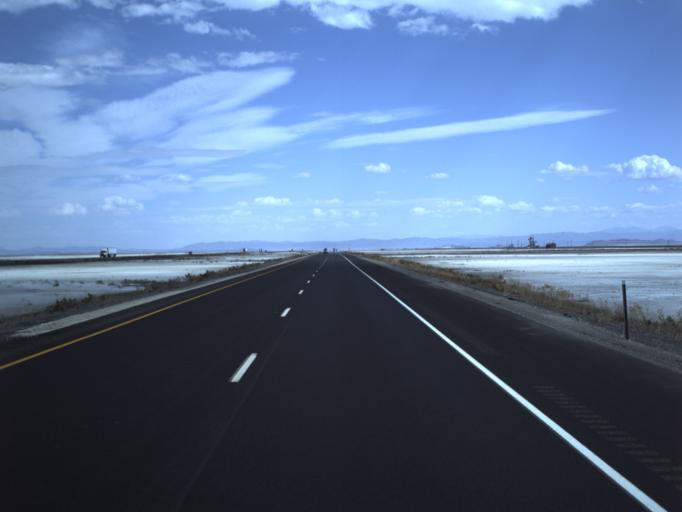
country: US
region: Utah
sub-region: Tooele County
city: Wendover
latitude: 40.7309
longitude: -113.4994
